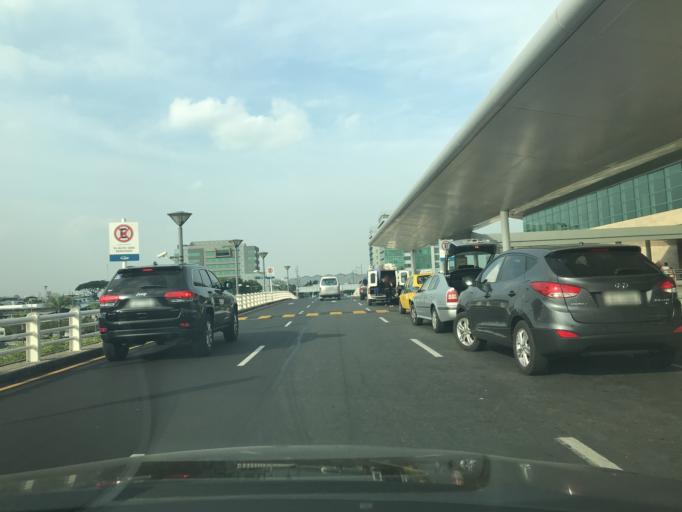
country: EC
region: Guayas
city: Eloy Alfaro
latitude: -2.1486
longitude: -79.8850
